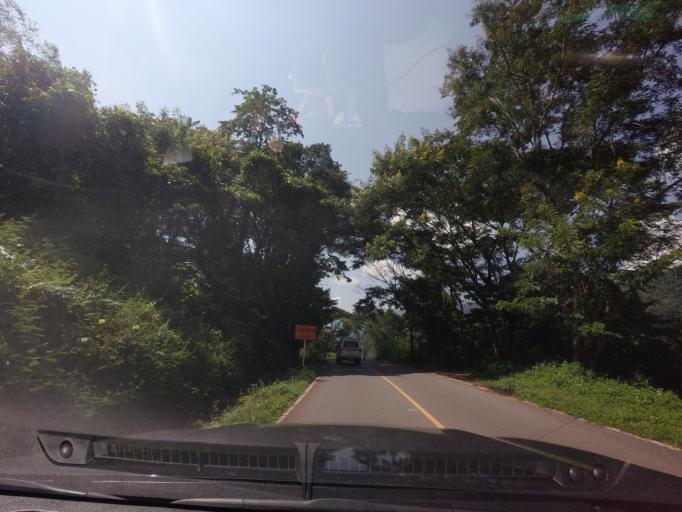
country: TH
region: Nan
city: Bo Kluea
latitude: 19.1485
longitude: 101.1554
